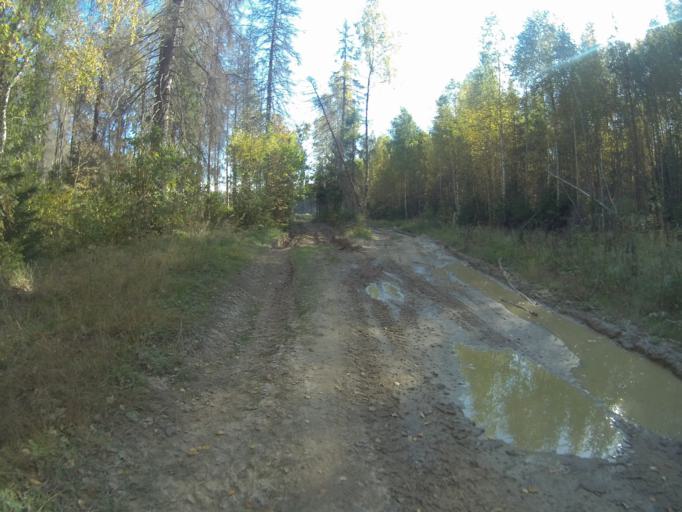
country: RU
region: Vladimir
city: Golovino
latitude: 55.9925
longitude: 40.4473
